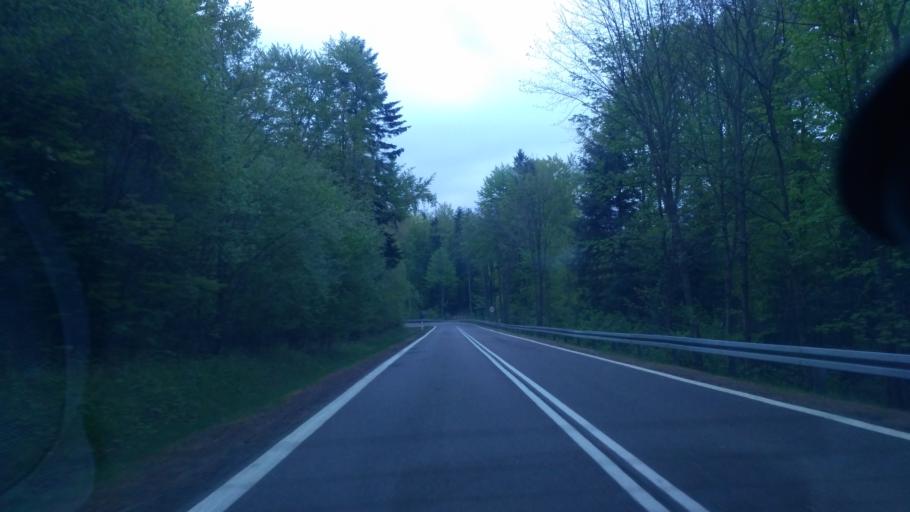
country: PL
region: Subcarpathian Voivodeship
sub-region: Powiat sanocki
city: Tyrawa Woloska
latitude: 49.5630
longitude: 22.3415
